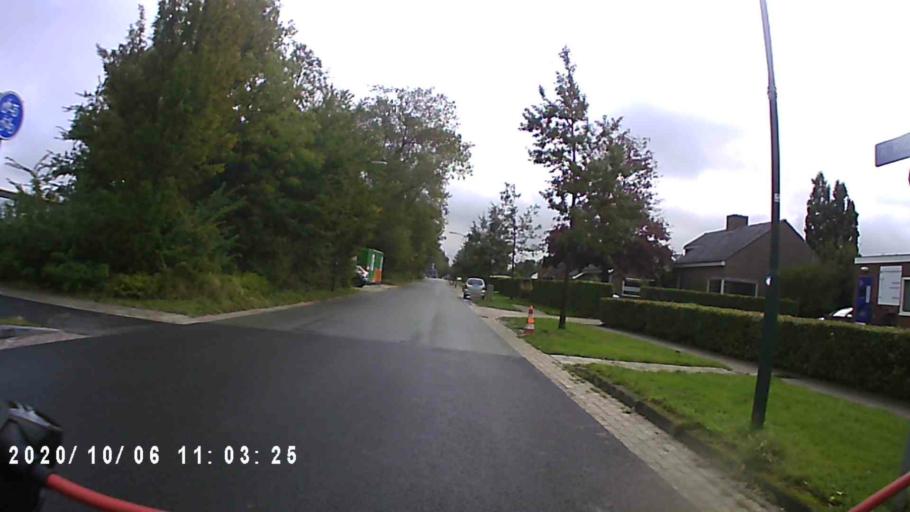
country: NL
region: Groningen
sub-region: Gemeente De Marne
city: Ulrum
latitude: 53.3625
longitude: 6.3736
